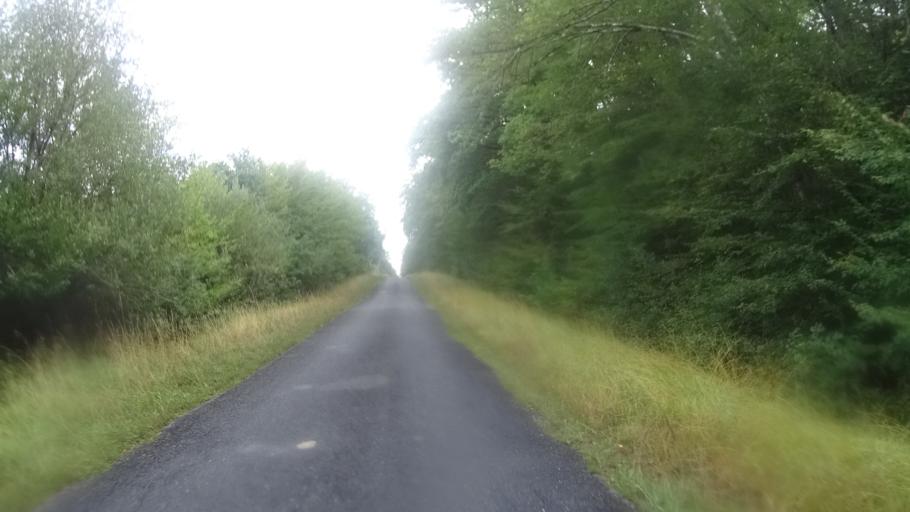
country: FR
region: Centre
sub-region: Departement du Loiret
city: Vitry-aux-Loges
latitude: 48.0143
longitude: 2.2484
